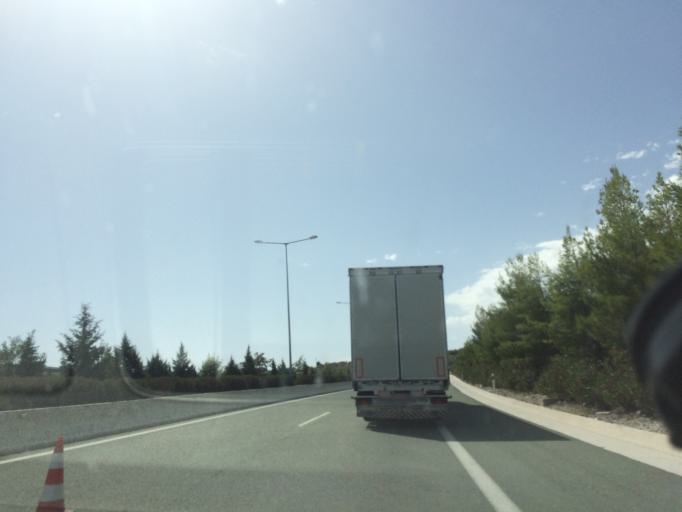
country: GR
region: Thessaly
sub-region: Nomos Magnisias
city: Pteleos
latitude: 39.0088
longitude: 22.9129
